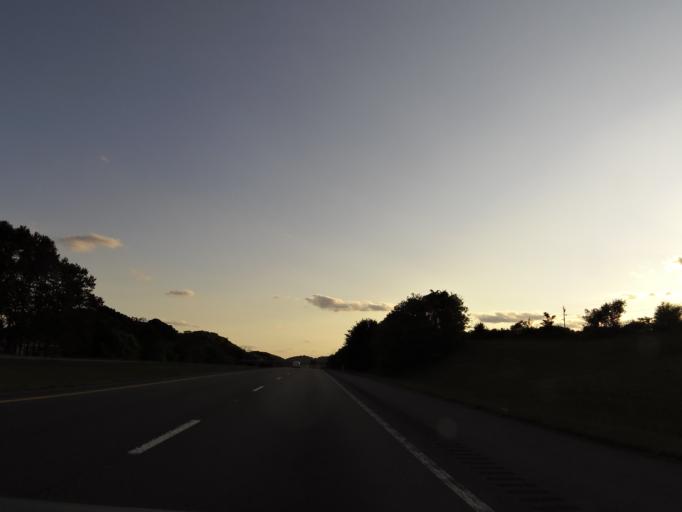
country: US
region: Tennessee
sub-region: Sullivan County
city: Walnut Hill
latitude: 36.5727
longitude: -82.2893
